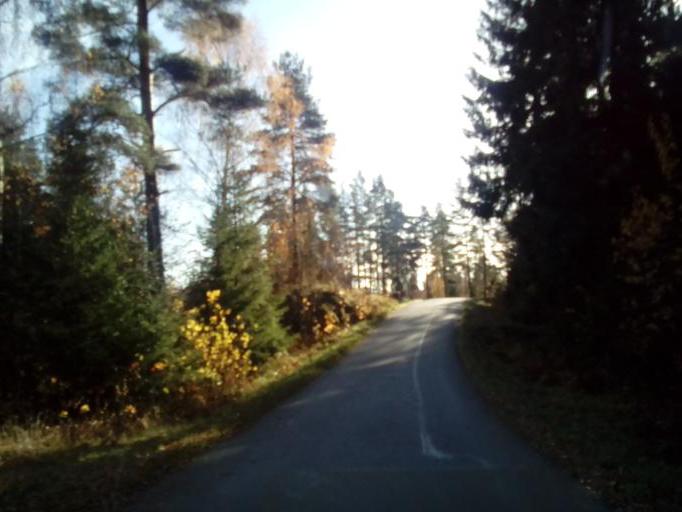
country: SE
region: Kalmar
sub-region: Vasterviks Kommun
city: Ankarsrum
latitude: 57.8044
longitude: 16.1679
